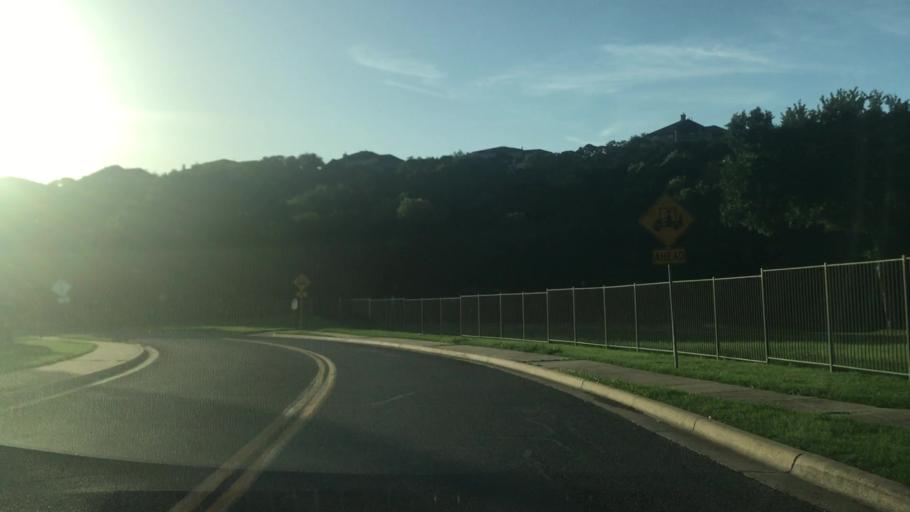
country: US
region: Texas
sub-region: Williamson County
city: Anderson Mill
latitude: 30.4508
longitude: -97.8536
